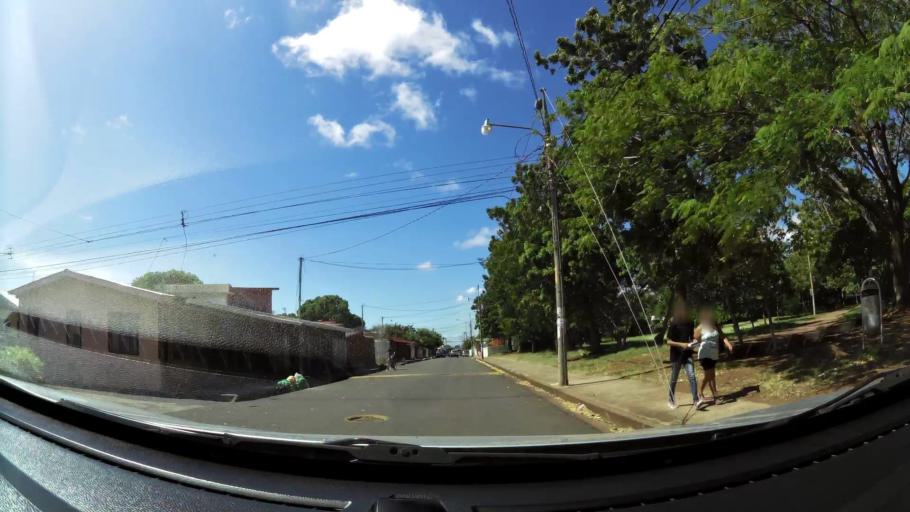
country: CR
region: Guanacaste
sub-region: Canton de Canas
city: Canas
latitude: 10.4283
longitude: -85.0880
